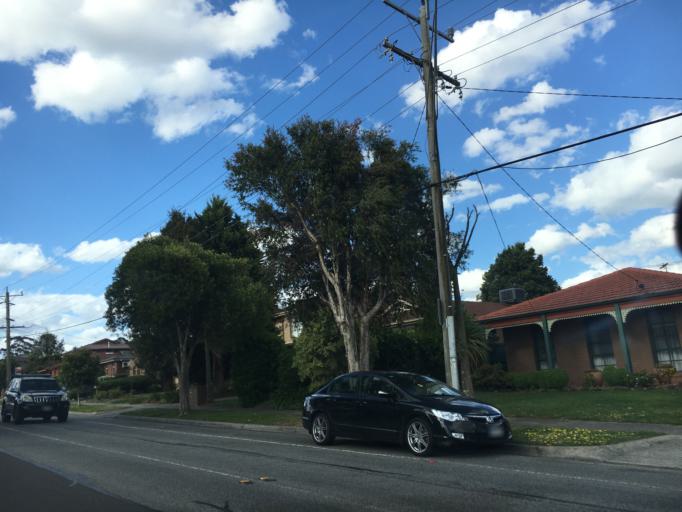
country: AU
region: Victoria
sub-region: Monash
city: Notting Hill
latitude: -37.8949
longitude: 145.1693
